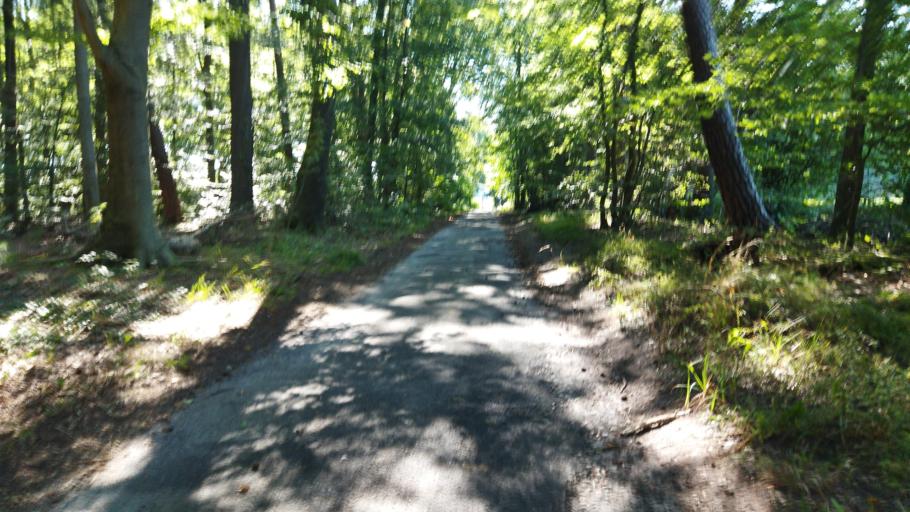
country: DE
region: Lower Saxony
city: Laar
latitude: 52.3742
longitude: 8.2386
